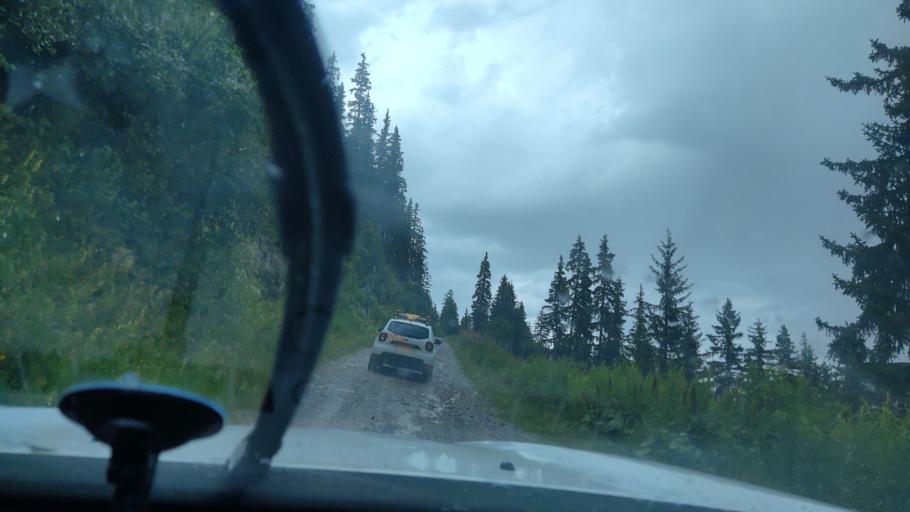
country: FR
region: Rhone-Alpes
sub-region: Departement de la Savoie
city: Courchevel
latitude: 45.3933
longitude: 6.6415
